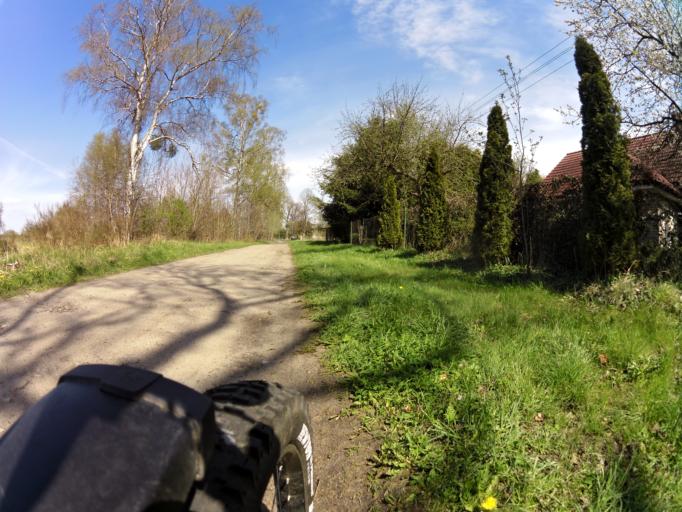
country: PL
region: West Pomeranian Voivodeship
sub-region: Powiat lobeski
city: Resko
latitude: 53.7968
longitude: 15.4412
